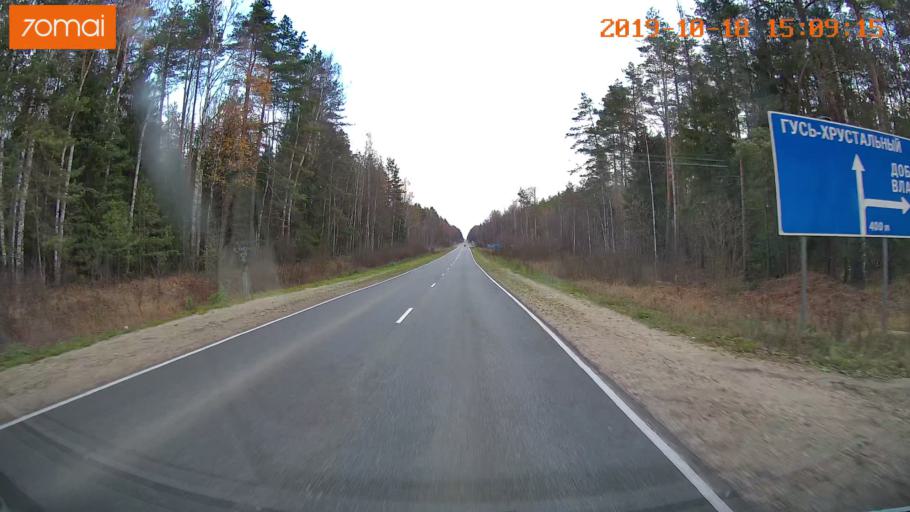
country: RU
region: Vladimir
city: Gus'-Khrustal'nyy
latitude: 55.5636
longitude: 40.6192
